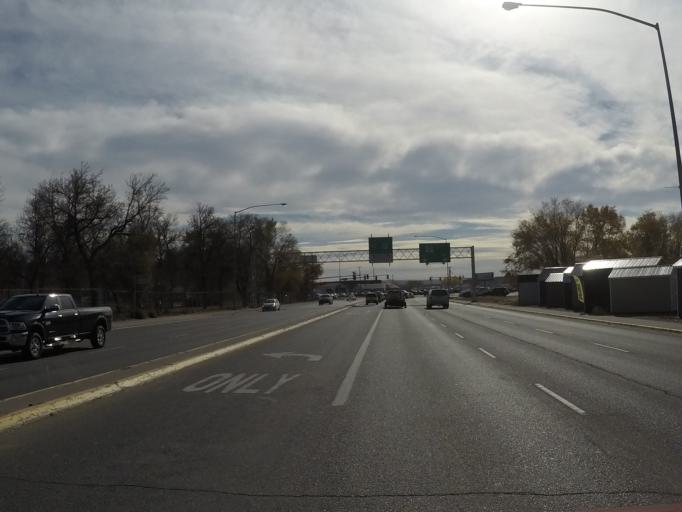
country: US
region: Montana
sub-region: Yellowstone County
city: Billings
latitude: 45.7959
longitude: -108.4814
